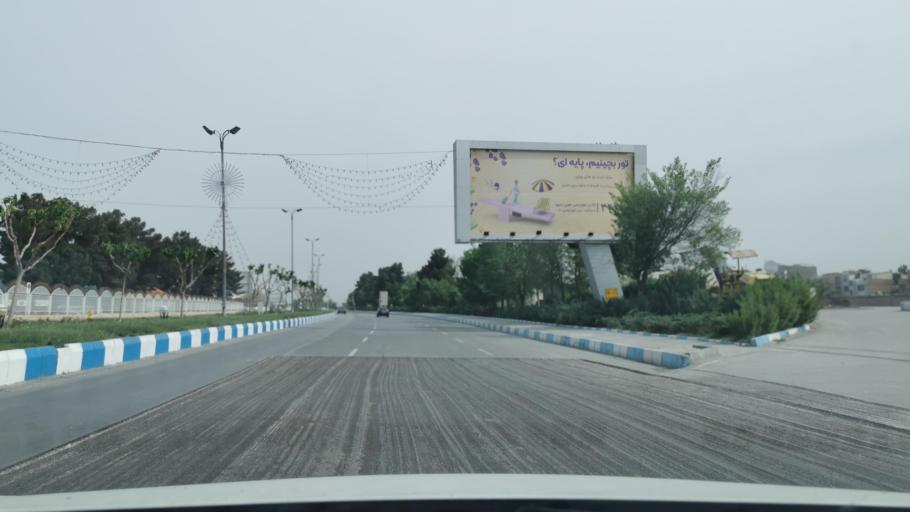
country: IR
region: Razavi Khorasan
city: Mashhad
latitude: 36.2354
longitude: 59.6312
